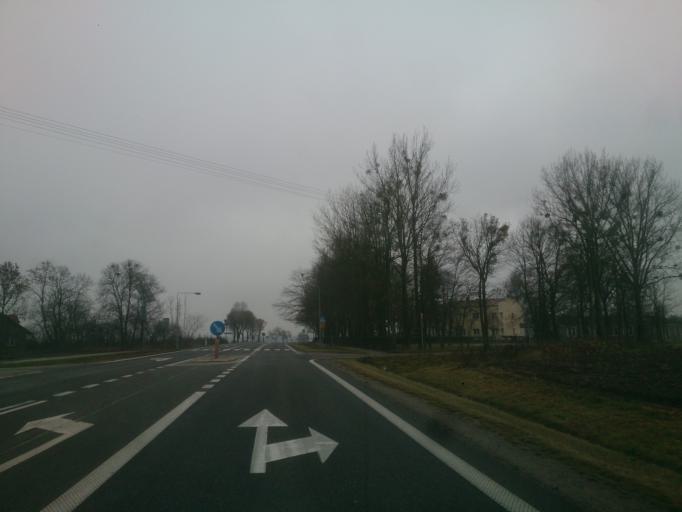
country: PL
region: Masovian Voivodeship
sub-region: Powiat plocki
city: Drobin
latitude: 52.6915
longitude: 20.0496
